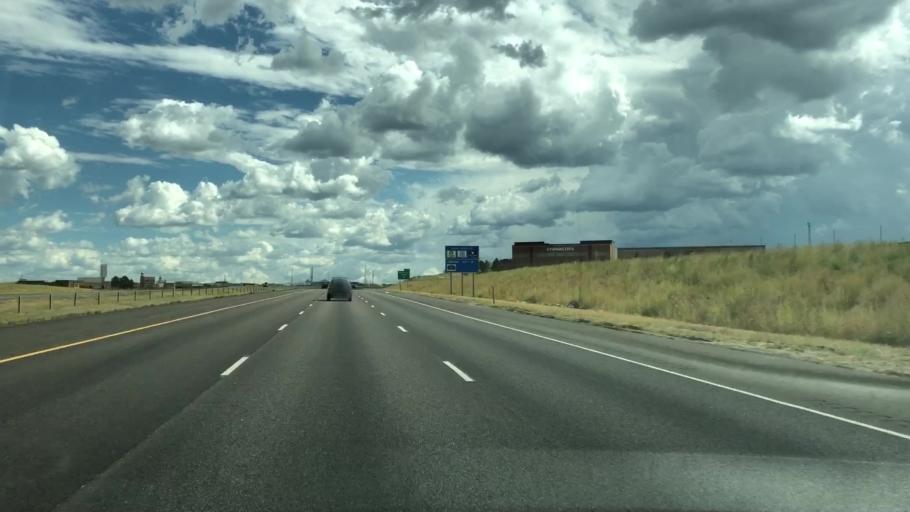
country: US
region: Colorado
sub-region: Douglas County
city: Parker
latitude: 39.6117
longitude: -104.7159
